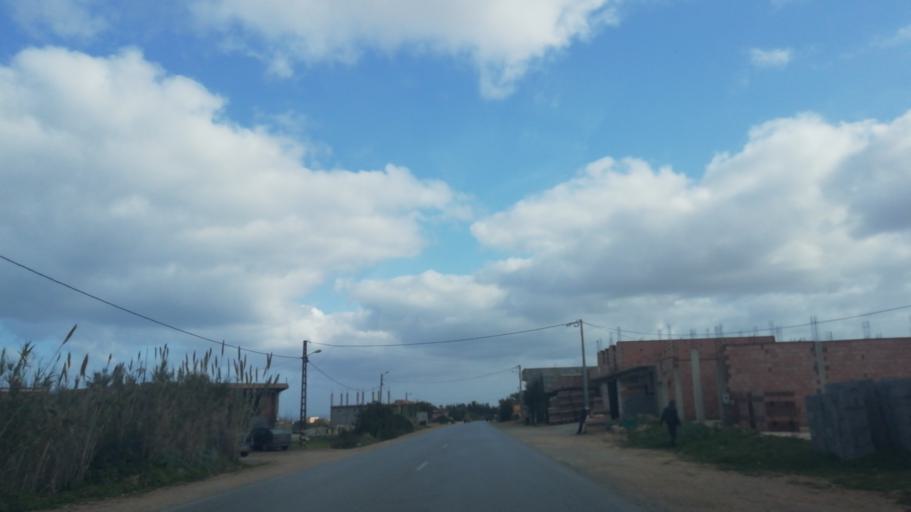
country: DZ
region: Relizane
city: Mazouna
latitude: 36.2769
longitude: 0.6364
